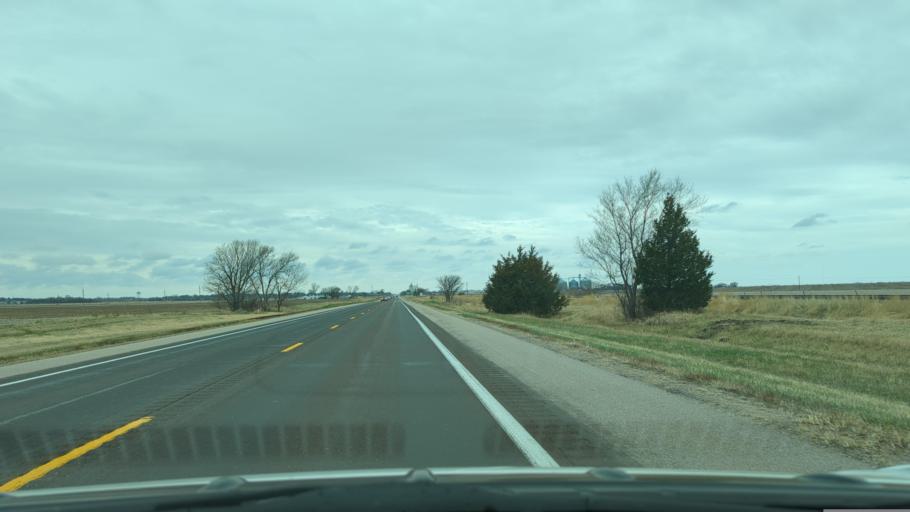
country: US
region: Nebraska
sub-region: Lancaster County
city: Waverly
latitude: 40.9336
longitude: -96.4951
